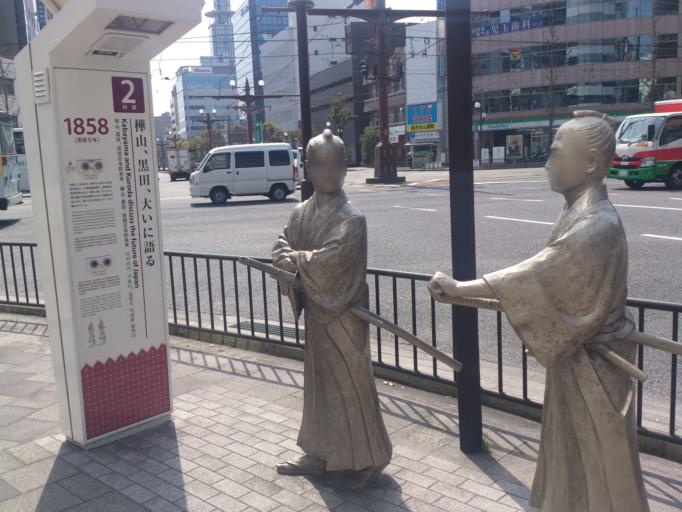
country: JP
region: Kagoshima
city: Kagoshima-shi
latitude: 31.5890
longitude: 130.5509
